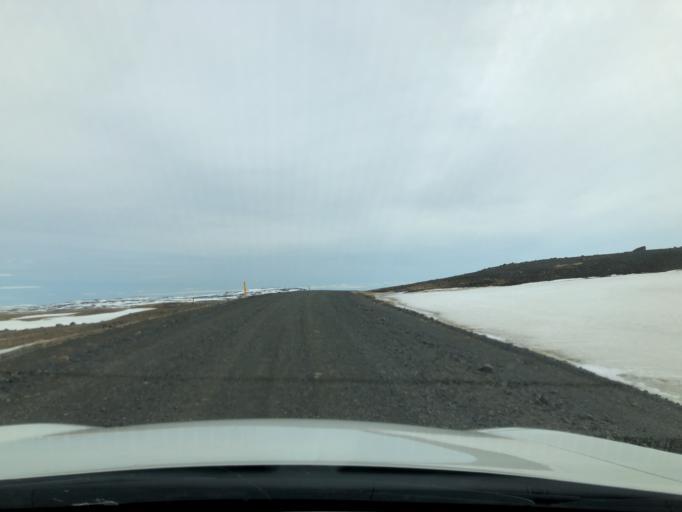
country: IS
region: East
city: Egilsstadir
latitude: 65.3088
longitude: -15.3813
